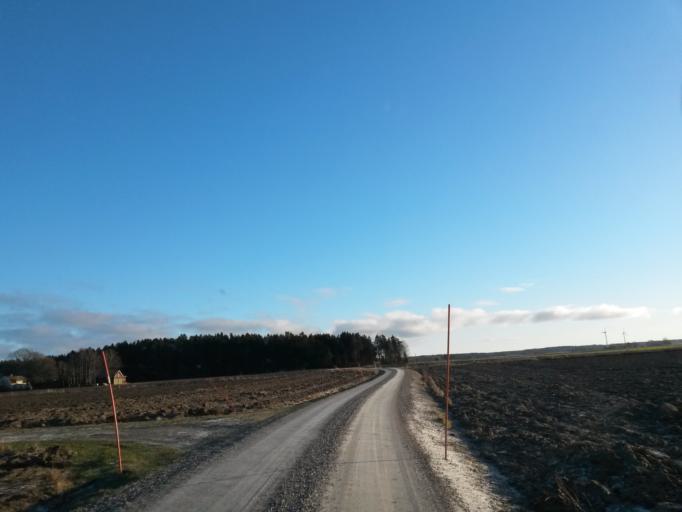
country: SE
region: Vaestra Goetaland
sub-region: Grastorps Kommun
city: Graestorp
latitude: 58.3791
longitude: 12.7953
